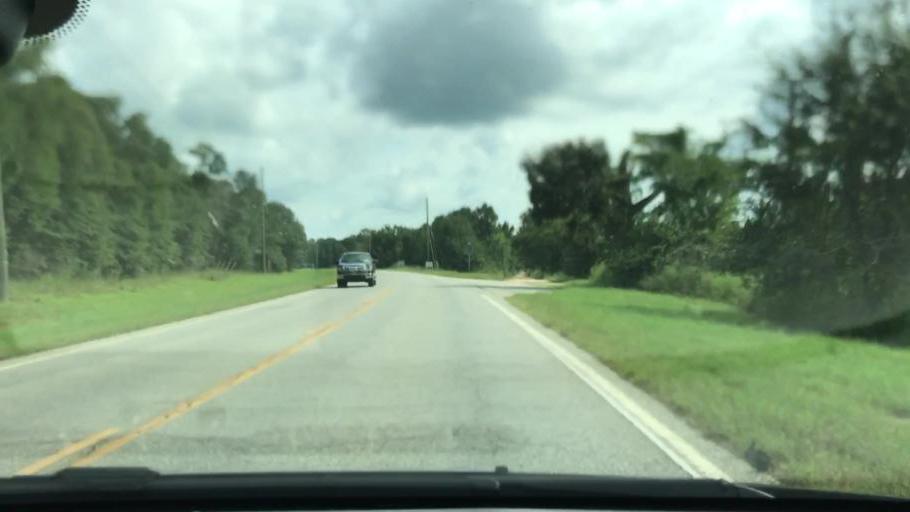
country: US
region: Georgia
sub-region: Clay County
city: Fort Gaines
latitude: 31.6538
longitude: -85.0474
